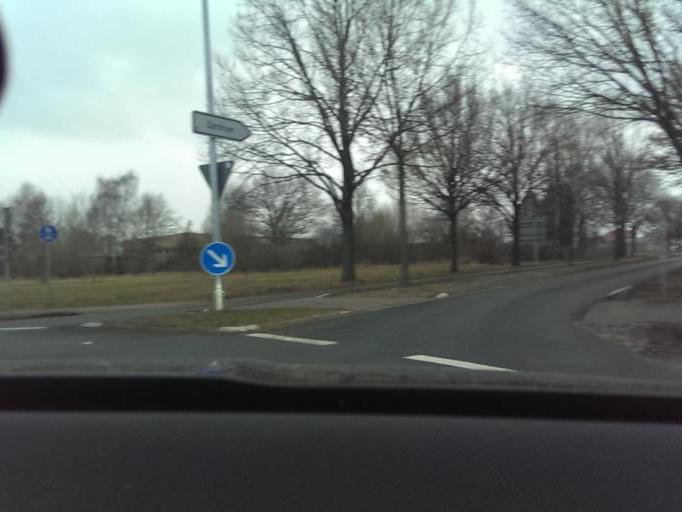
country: DE
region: Lower Saxony
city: Isernhagen Farster Bauerschaft
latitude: 52.4816
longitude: 9.8579
